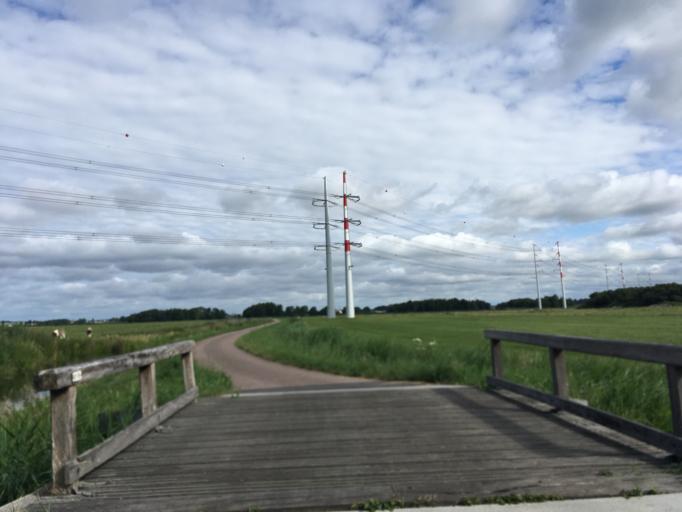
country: NL
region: North Holland
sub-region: Gemeente Haarlem
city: Haarlem
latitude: 52.3864
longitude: 4.7026
